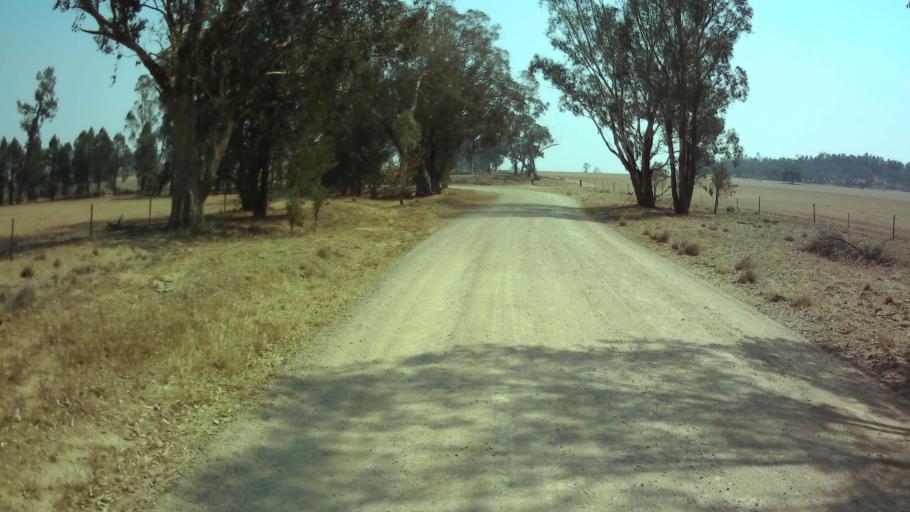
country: AU
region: New South Wales
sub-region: Weddin
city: Grenfell
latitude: -33.6472
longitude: 148.2703
